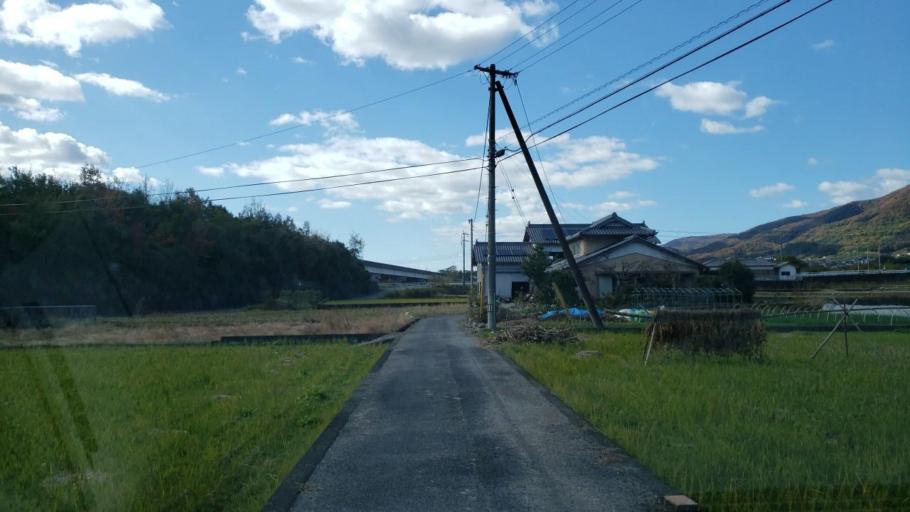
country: JP
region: Tokushima
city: Wakimachi
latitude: 34.0776
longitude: 134.1776
